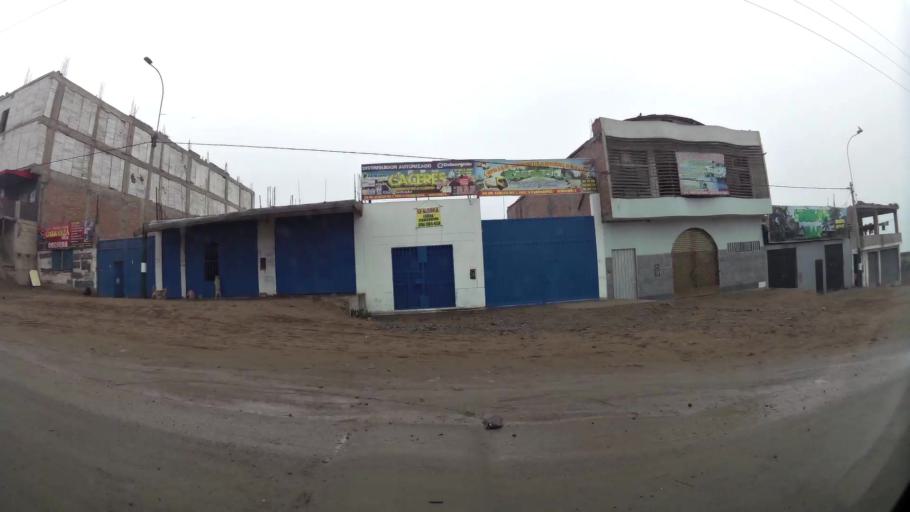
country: PE
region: Lima
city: Ventanilla
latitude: -11.8385
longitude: -77.1397
